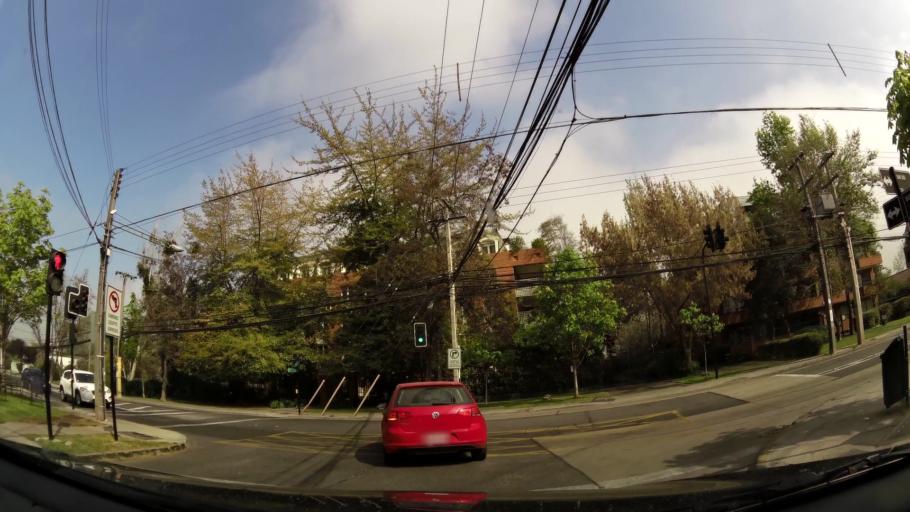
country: CL
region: Santiago Metropolitan
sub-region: Provincia de Santiago
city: Villa Presidente Frei, Nunoa, Santiago, Chile
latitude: -33.3866
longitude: -70.5707
